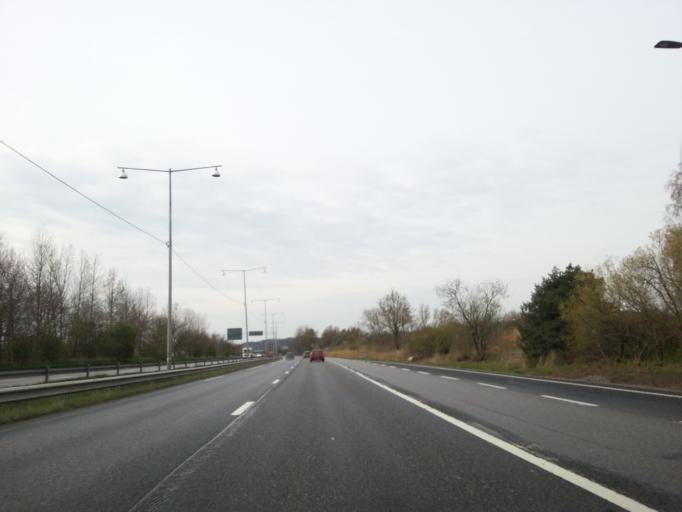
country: SE
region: Vaestra Goetaland
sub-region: Goteborg
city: Gardsten
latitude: 57.7934
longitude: 12.0032
